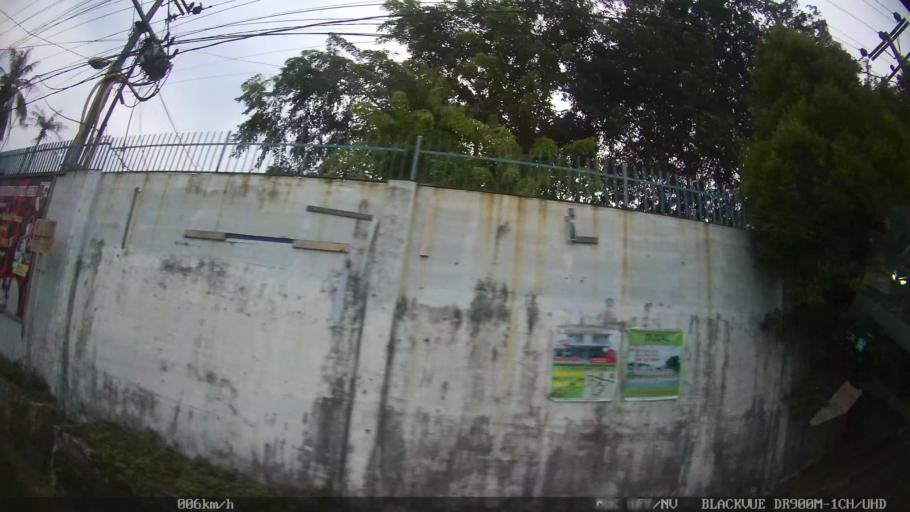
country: ID
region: North Sumatra
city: Sunggal
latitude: 3.5935
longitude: 98.6024
